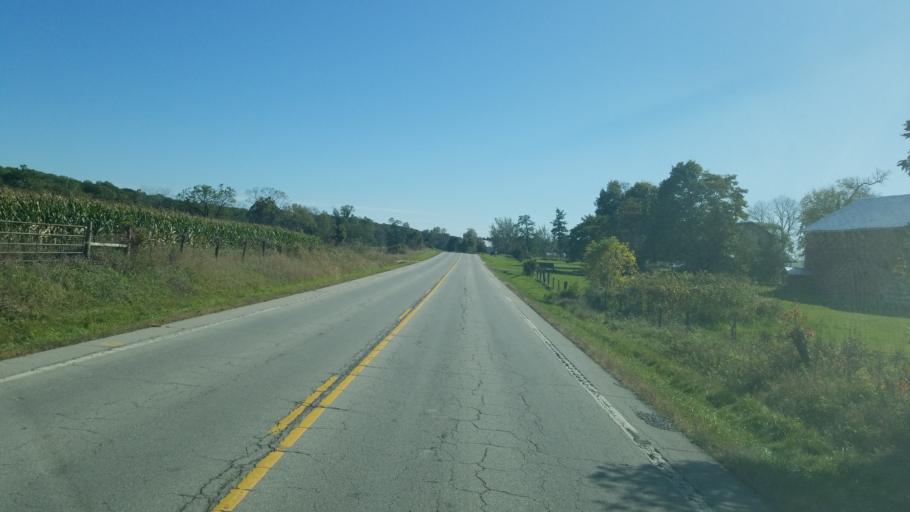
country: US
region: Ohio
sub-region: Huron County
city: New London
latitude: 41.0079
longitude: -82.4041
